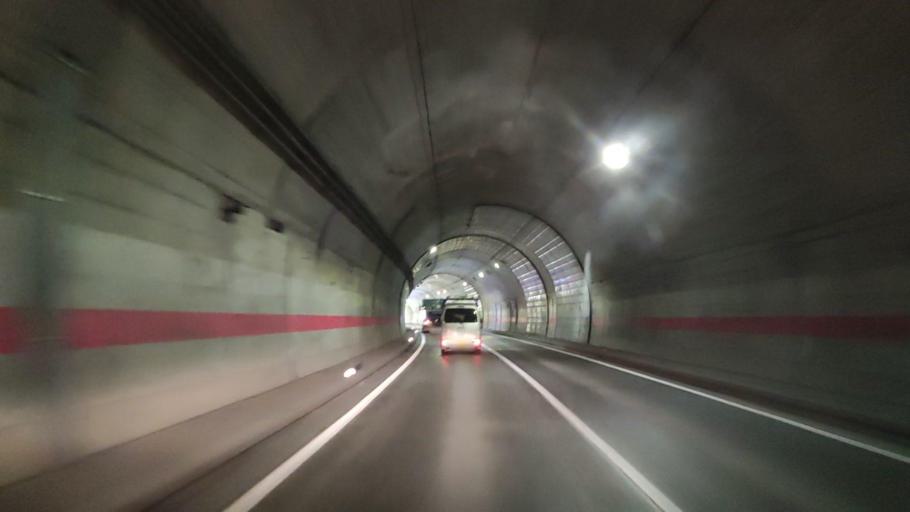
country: JP
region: Gifu
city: Takayama
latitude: 36.2562
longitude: 137.4736
